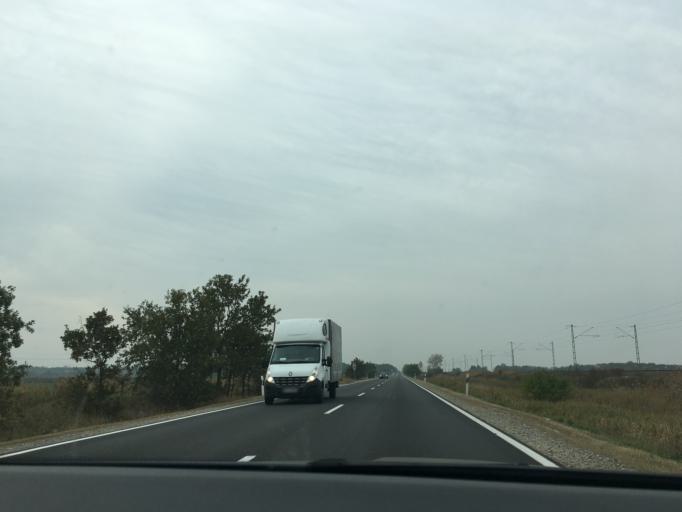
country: HU
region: Hajdu-Bihar
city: Puspokladany
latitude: 47.3182
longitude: 21.0351
